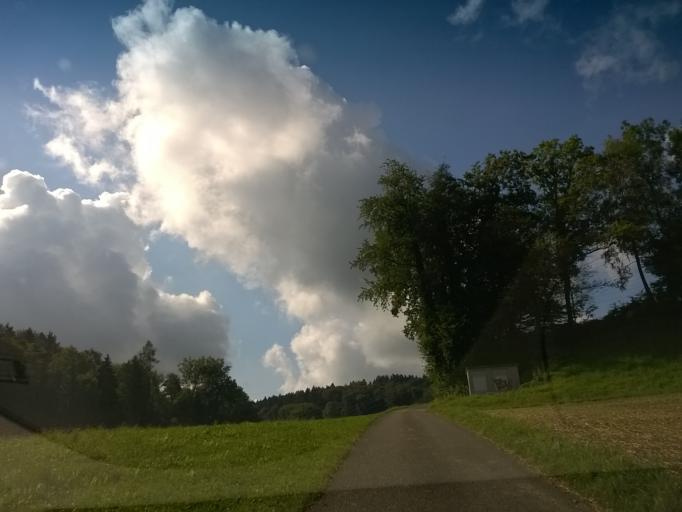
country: CH
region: Zurich
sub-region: Bezirk Winterthur
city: Pfungen
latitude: 47.4879
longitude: 8.6276
